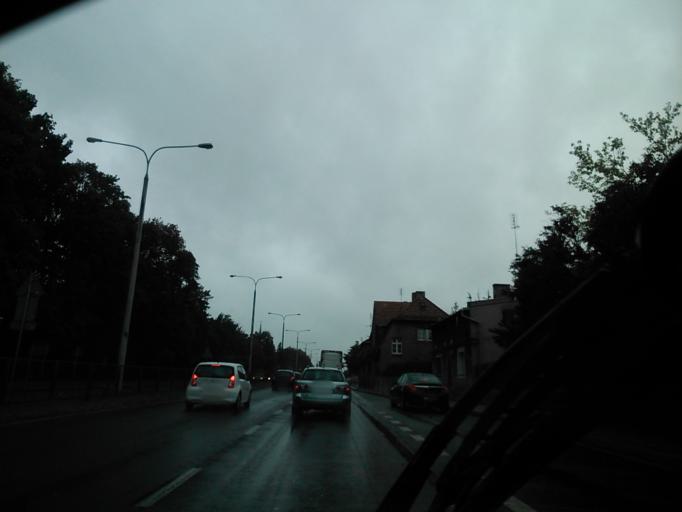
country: PL
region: Greater Poland Voivodeship
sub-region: Powiat gnieznienski
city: Gniezno
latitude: 52.5347
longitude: 17.5804
